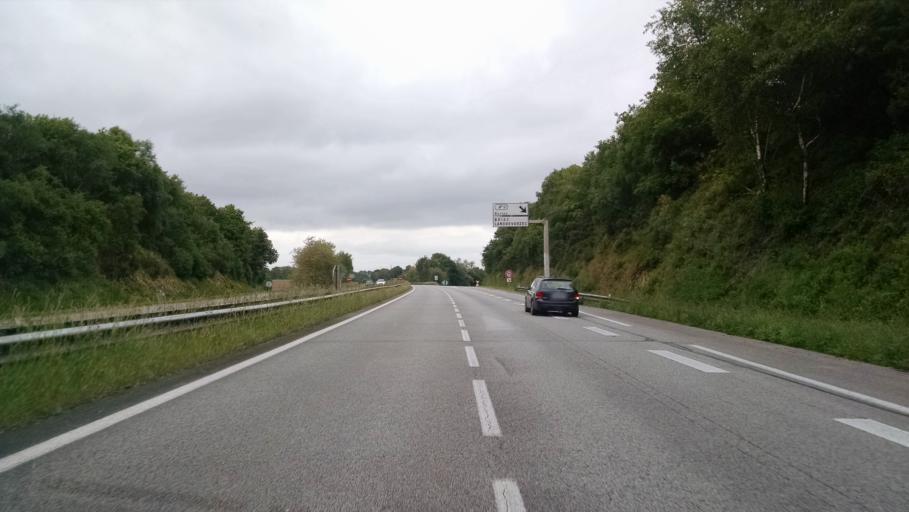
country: FR
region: Brittany
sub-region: Departement du Finistere
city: Landrevarzec
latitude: 48.0966
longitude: -4.0325
